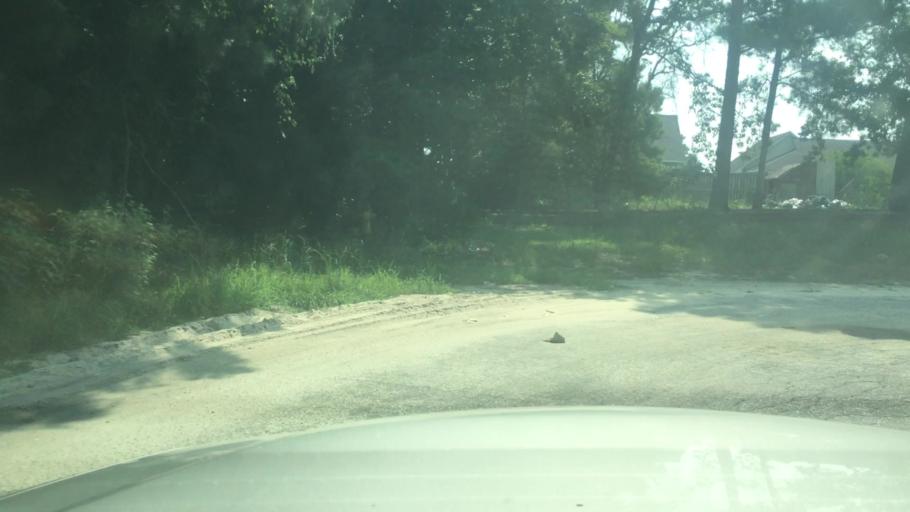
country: US
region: North Carolina
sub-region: Cumberland County
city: Hope Mills
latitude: 35.0020
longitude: -78.9477
